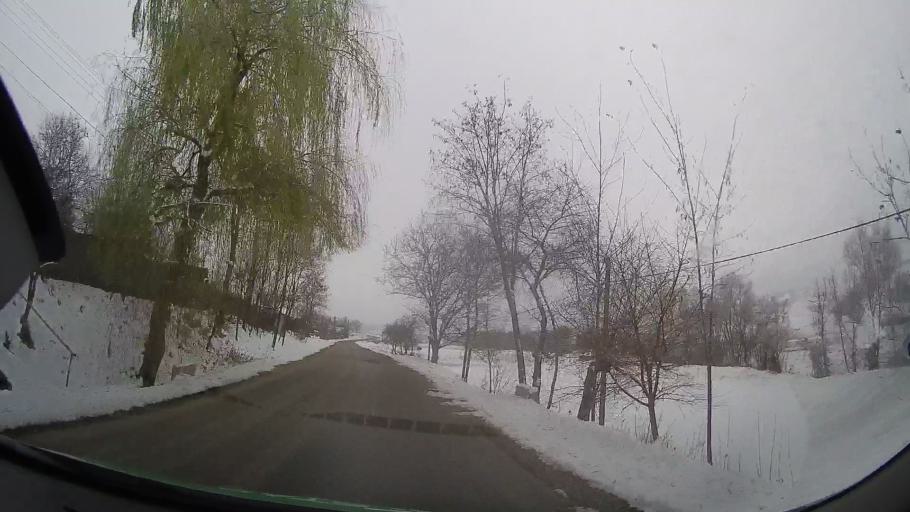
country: RO
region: Bacau
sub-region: Comuna Vultureni
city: Vultureni
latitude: 46.3820
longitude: 27.2762
